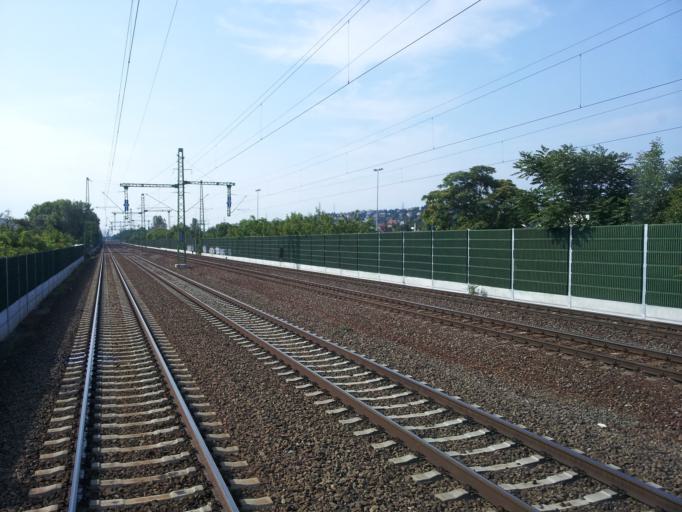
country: HU
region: Budapest
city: Budapest XXII. keruelet
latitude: 47.4506
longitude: 19.0276
